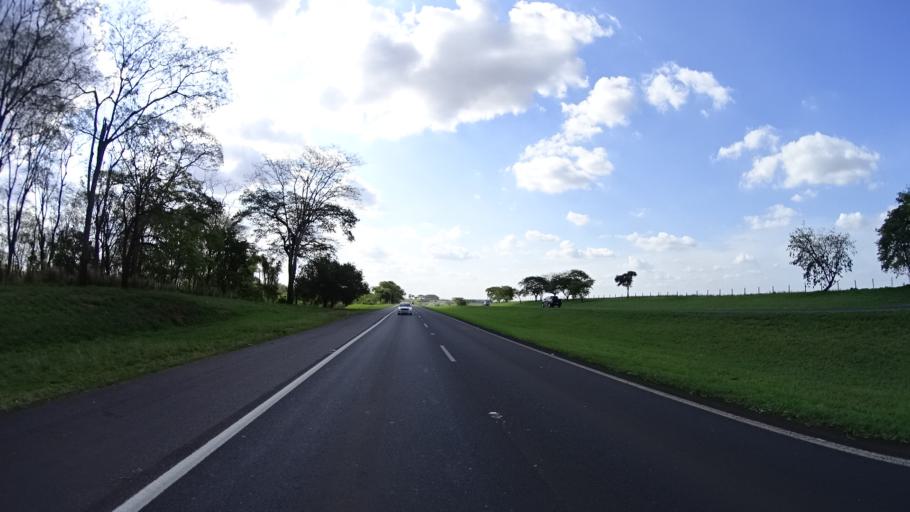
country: BR
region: Sao Paulo
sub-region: Guapiacu
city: Guapiacu
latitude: -20.9617
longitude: -49.2431
